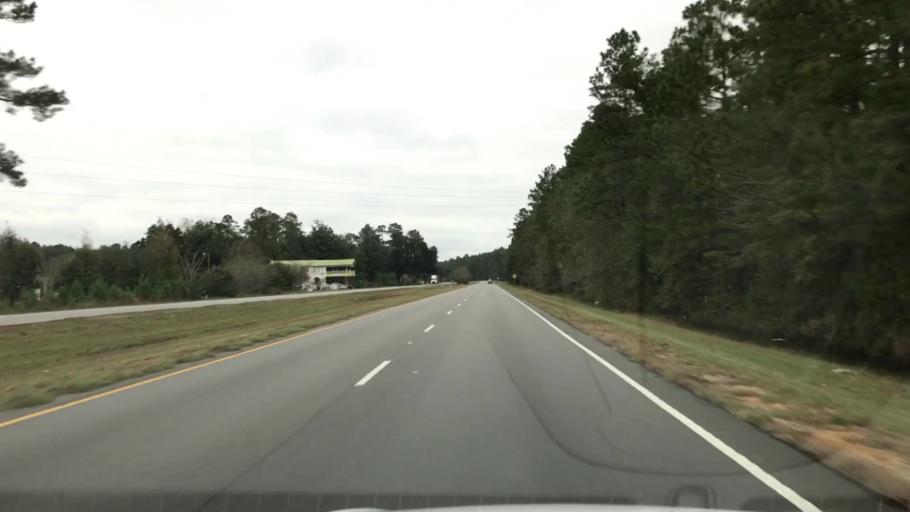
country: US
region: South Carolina
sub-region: Georgetown County
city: Georgetown
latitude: 33.2262
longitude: -79.3775
